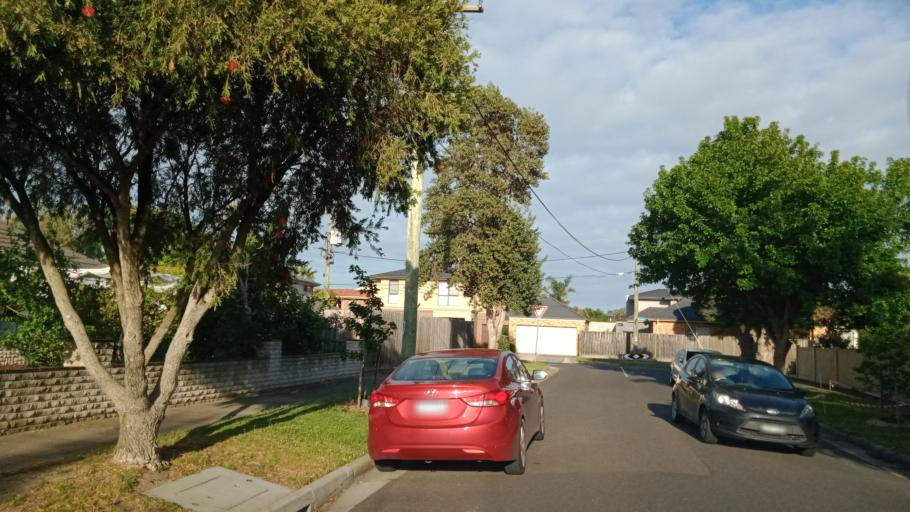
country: AU
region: Victoria
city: McKinnon
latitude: -37.9269
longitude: 145.0529
